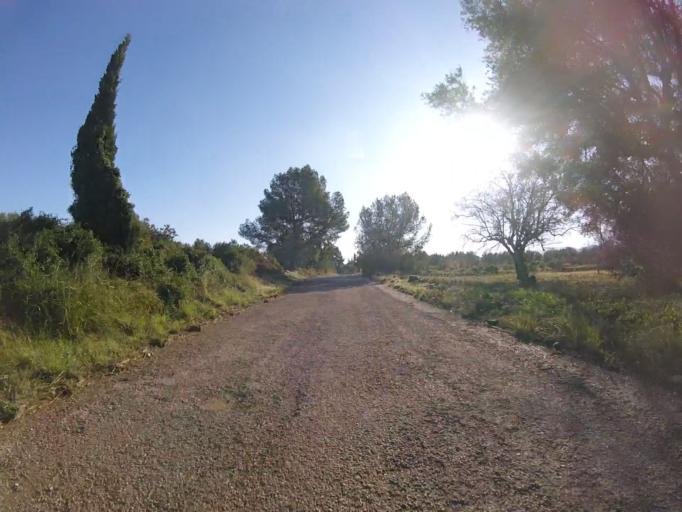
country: ES
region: Valencia
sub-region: Provincia de Castello
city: Peniscola
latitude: 40.3908
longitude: 0.3682
